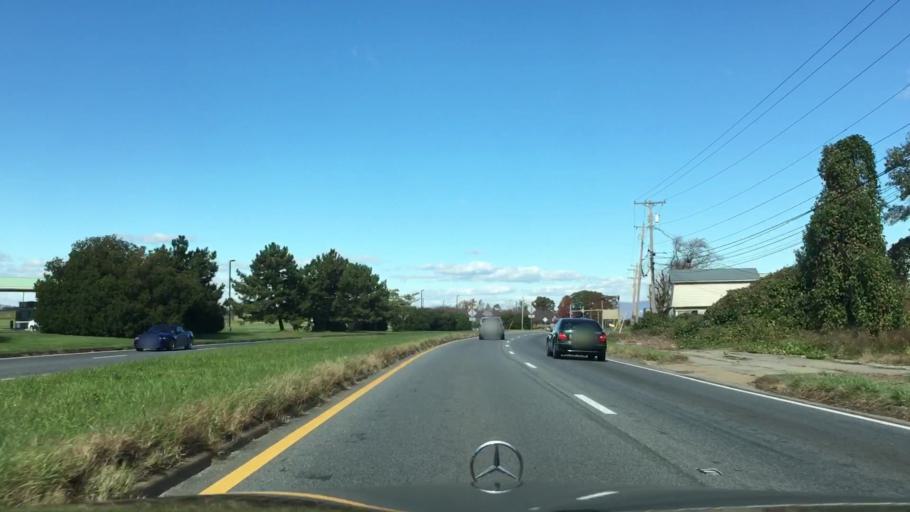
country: US
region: Virginia
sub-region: Campbell County
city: Timberlake
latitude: 37.3310
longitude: -79.1916
